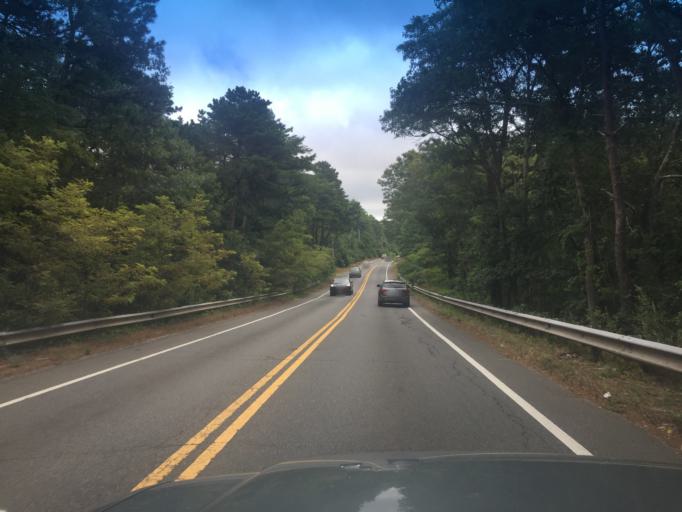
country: US
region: Massachusetts
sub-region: Barnstable County
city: Marstons Mills
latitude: 41.6529
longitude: -70.4016
